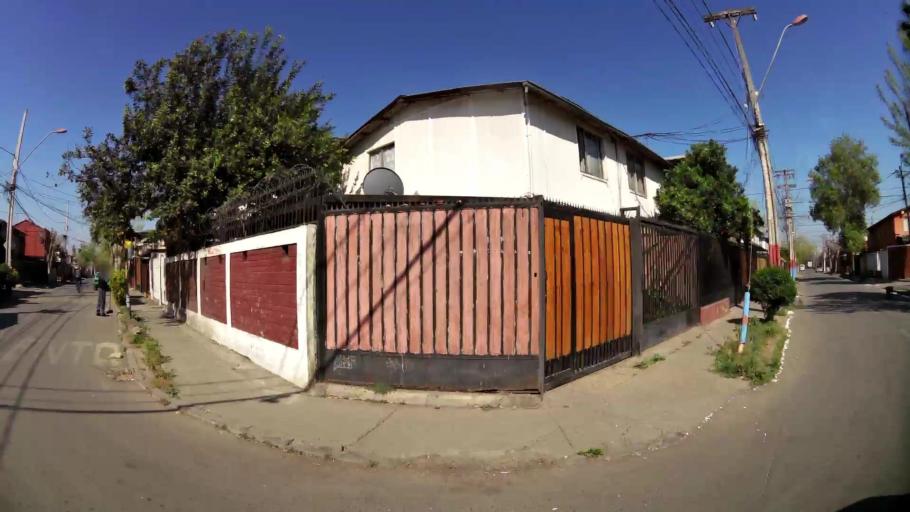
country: CL
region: Santiago Metropolitan
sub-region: Provincia de Chacabuco
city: Chicureo Abajo
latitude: -33.3560
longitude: -70.6866
